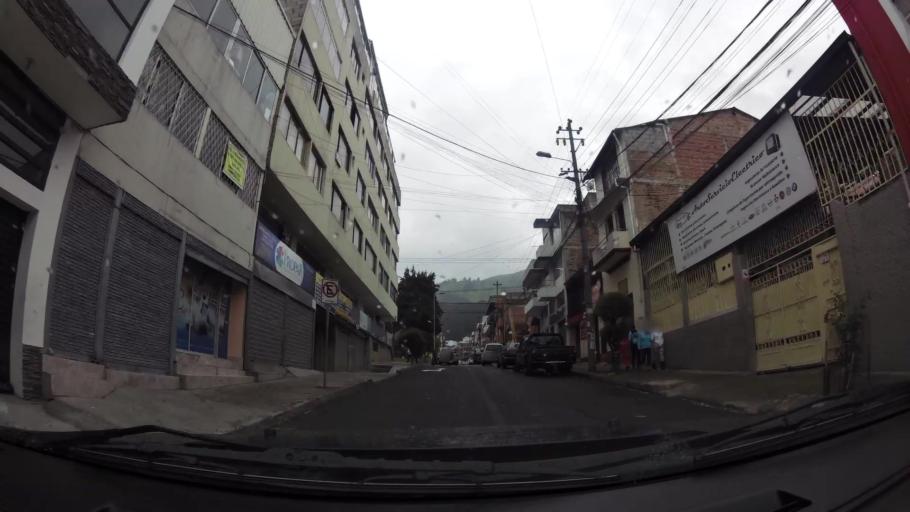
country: EC
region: Pichincha
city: Quito
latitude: -0.2078
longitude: -78.5044
